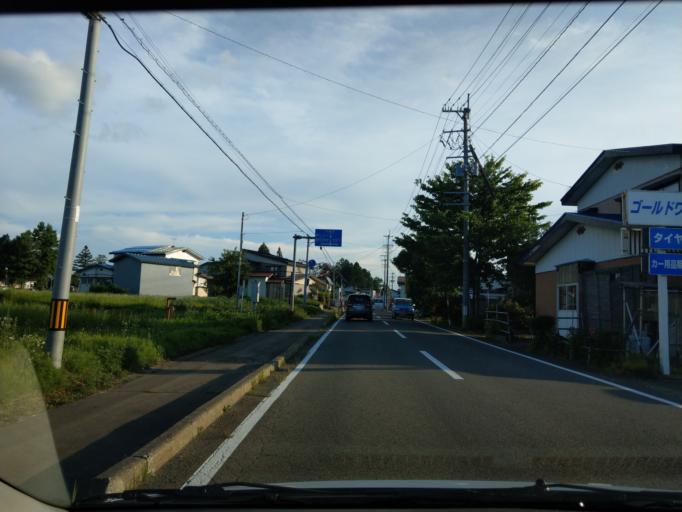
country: JP
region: Akita
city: Omagari
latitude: 39.4379
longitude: 140.5636
